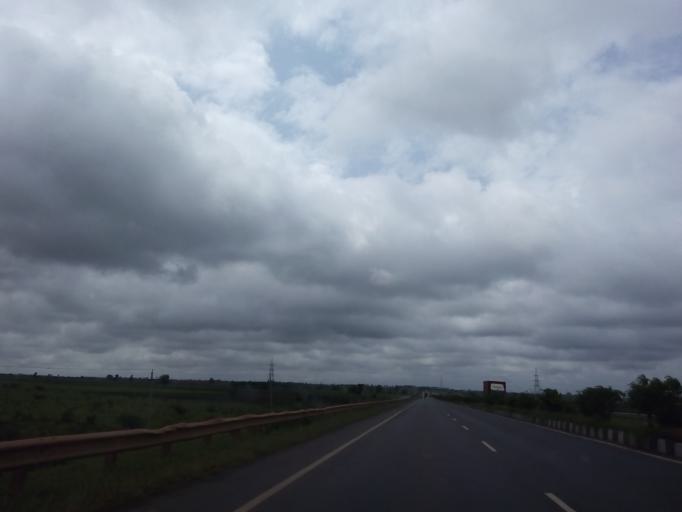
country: IN
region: Karnataka
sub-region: Haveri
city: Haveri
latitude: 14.8377
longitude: 75.3546
